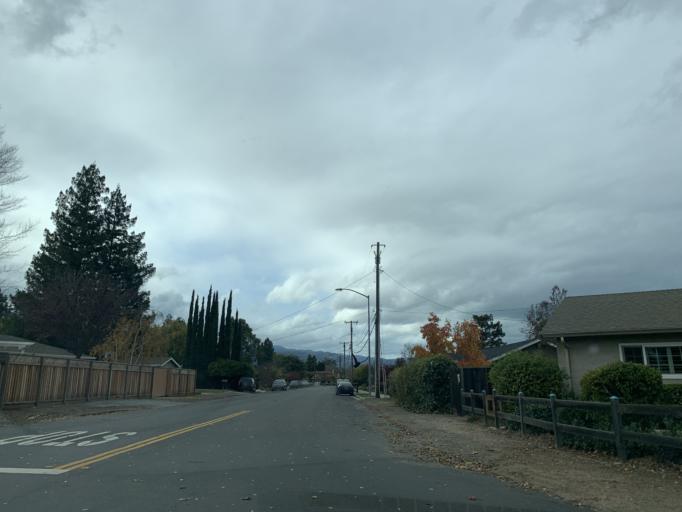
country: US
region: California
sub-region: Santa Clara County
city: Campbell
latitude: 37.2660
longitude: -121.9703
